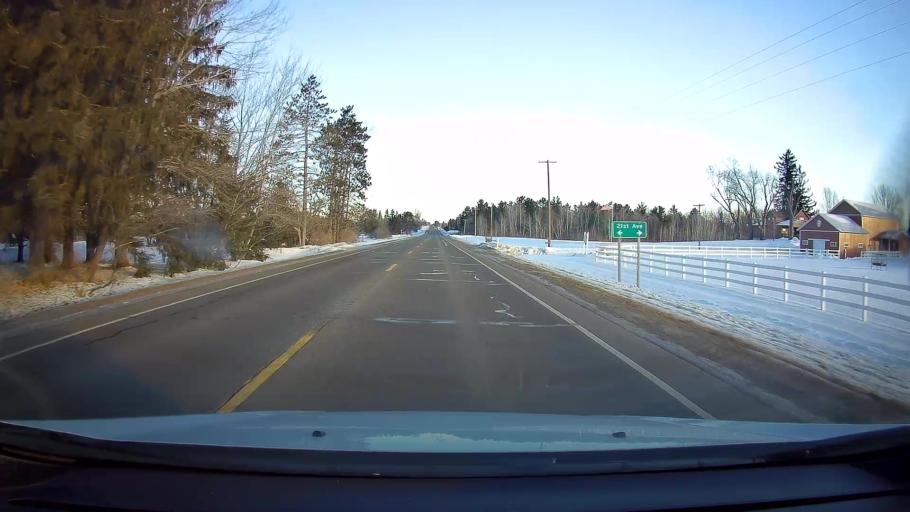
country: US
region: Wisconsin
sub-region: Barron County
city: Cumberland
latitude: 45.5077
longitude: -92.0523
